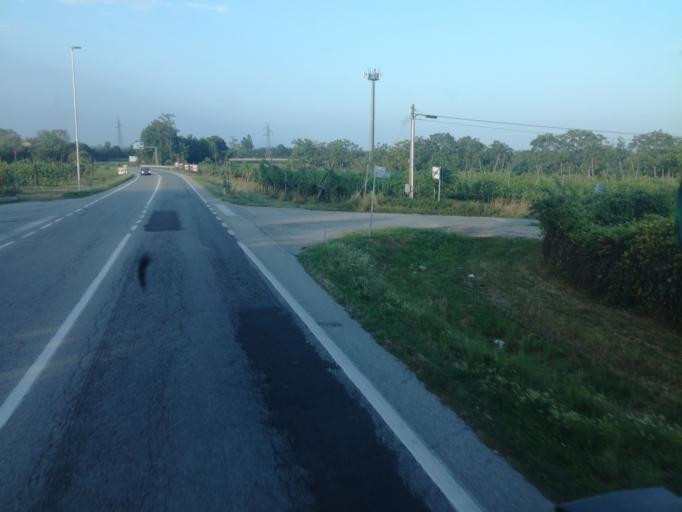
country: IT
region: Piedmont
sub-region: Provincia di Torino
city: Bricherasio
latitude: 44.8222
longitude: 7.3094
